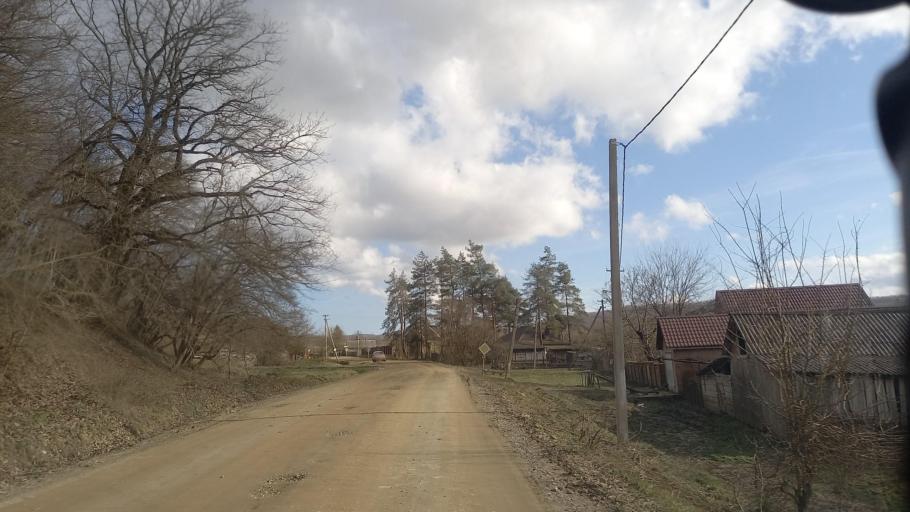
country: RU
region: Krasnodarskiy
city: Smolenskaya
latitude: 44.6053
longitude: 38.8465
